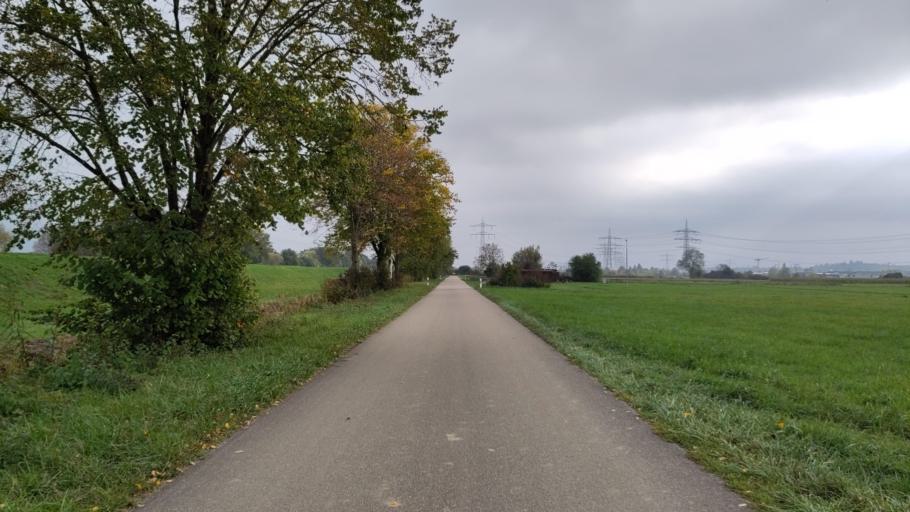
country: DE
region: Baden-Wuerttemberg
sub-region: Freiburg Region
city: Riegel
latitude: 48.1354
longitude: 7.7566
